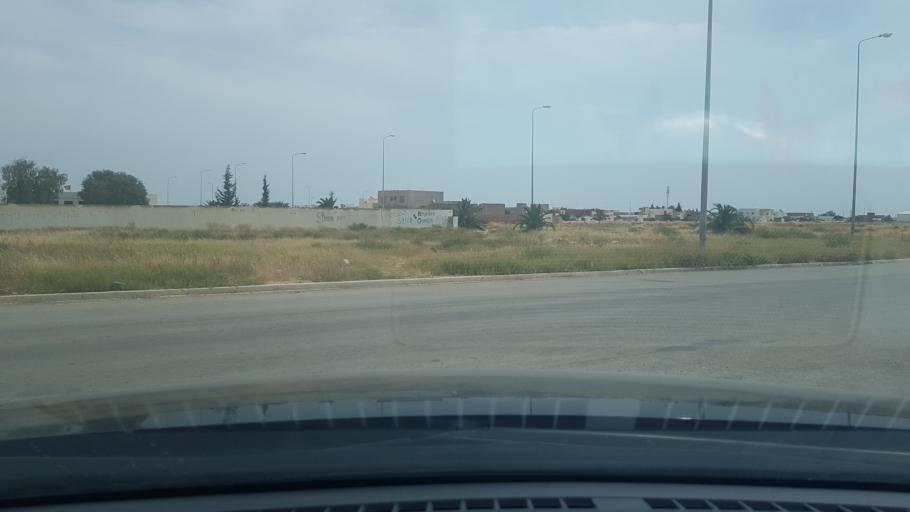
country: TN
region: Safaqis
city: Al Qarmadah
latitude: 34.8248
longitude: 10.7420
